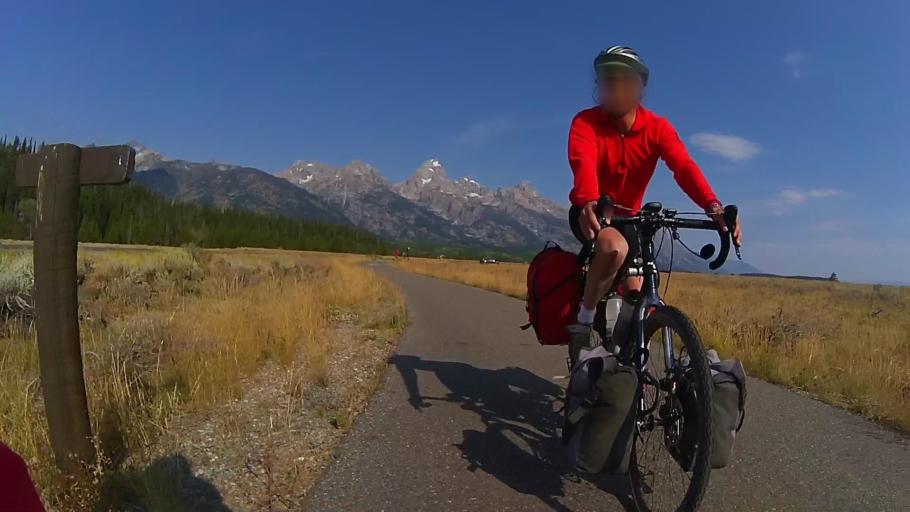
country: US
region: Wyoming
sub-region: Teton County
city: Moose Wilson Road
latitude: 43.6762
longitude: -110.7237
